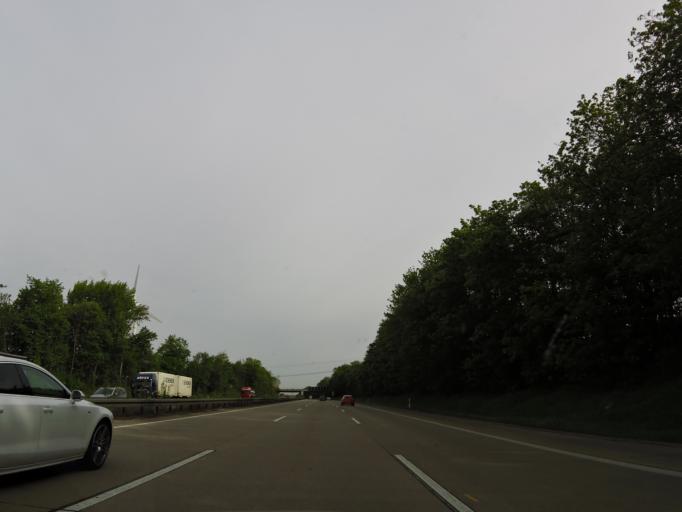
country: DE
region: Lower Saxony
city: Algermissen
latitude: 52.2705
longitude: 9.9141
